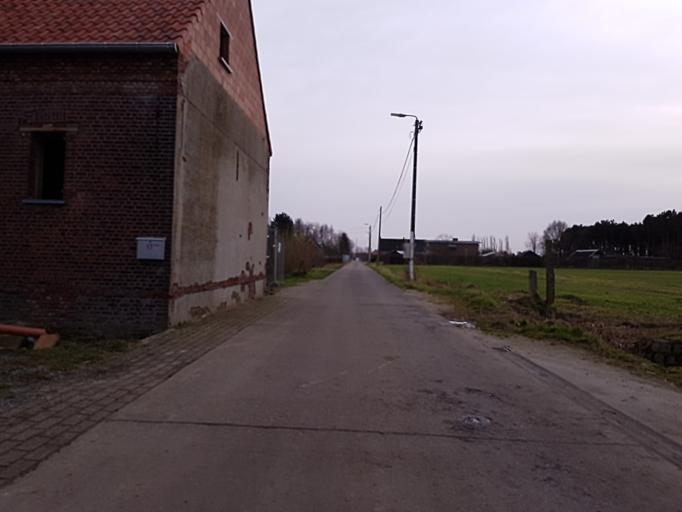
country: BE
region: Flanders
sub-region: Provincie Antwerpen
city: Putte
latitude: 51.0502
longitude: 4.6374
